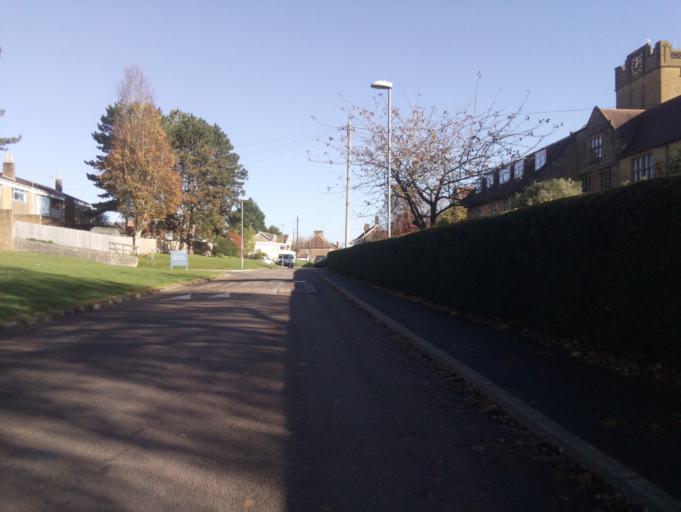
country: GB
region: England
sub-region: Dorset
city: Sherborne
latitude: 50.9487
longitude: -2.5276
